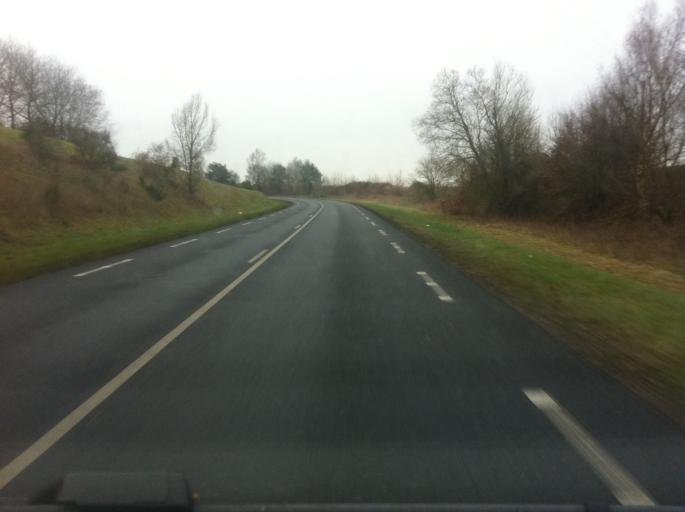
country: FR
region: Haute-Normandie
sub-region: Departement de la Seine-Maritime
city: La Mailleraye-sur-Seine
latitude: 49.4651
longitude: 0.7716
